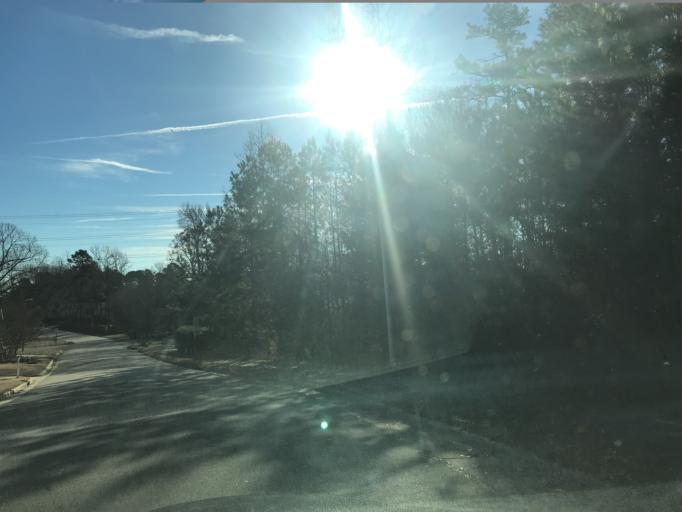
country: US
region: North Carolina
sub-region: Wake County
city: West Raleigh
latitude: 35.8966
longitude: -78.6040
